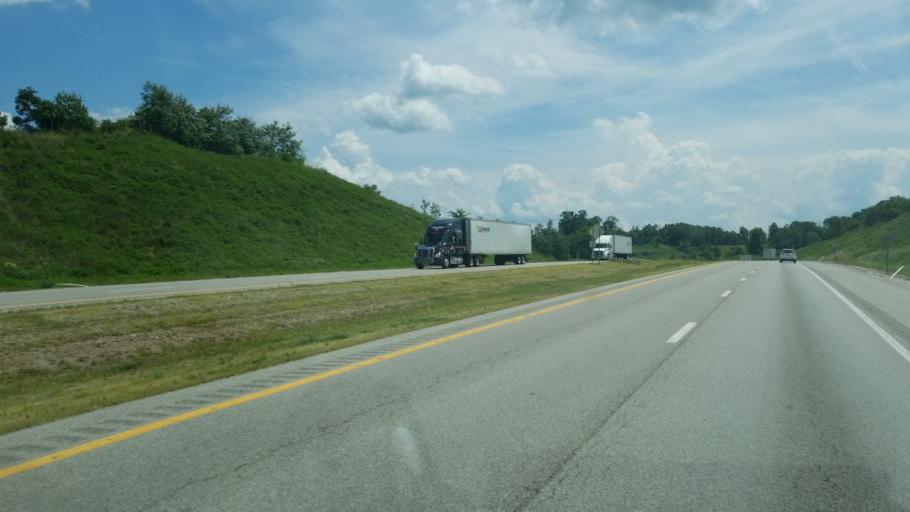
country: US
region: West Virginia
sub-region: Mason County
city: Point Pleasant
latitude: 38.7938
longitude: -82.0961
